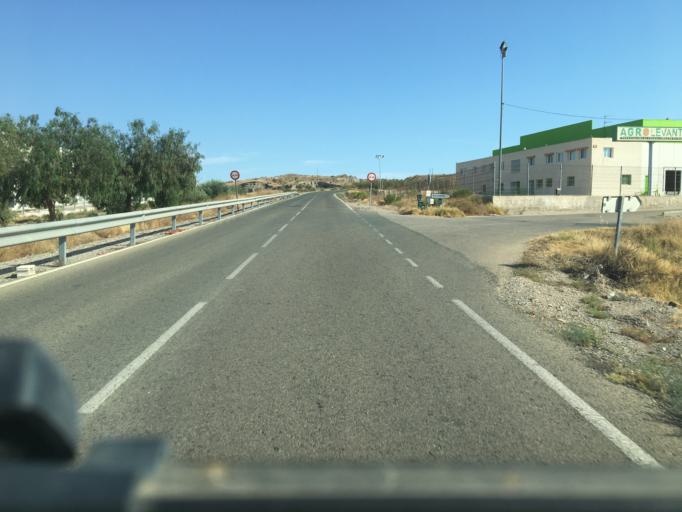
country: ES
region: Andalusia
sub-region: Provincia de Almeria
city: Huercal-Overa
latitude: 37.4195
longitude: -1.9687
